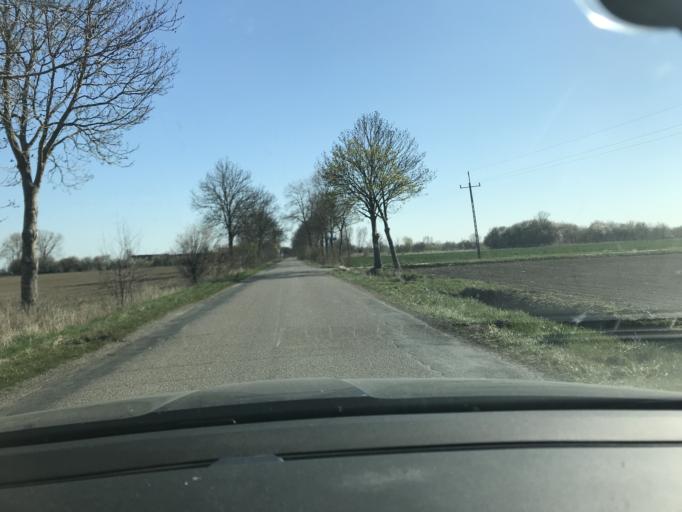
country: PL
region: Pomeranian Voivodeship
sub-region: Powiat nowodworski
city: Sztutowo
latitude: 54.3204
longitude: 19.1585
